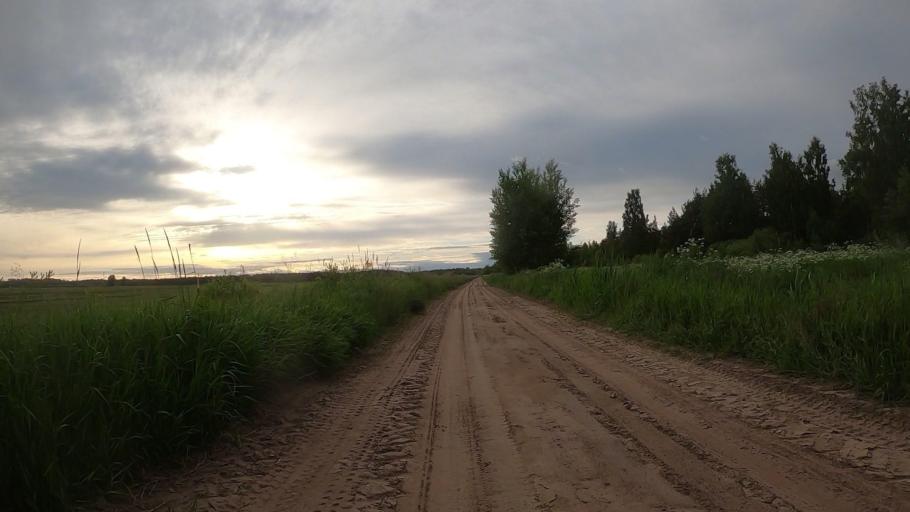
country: LV
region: Olaine
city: Olaine
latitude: 56.8241
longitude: 23.9692
